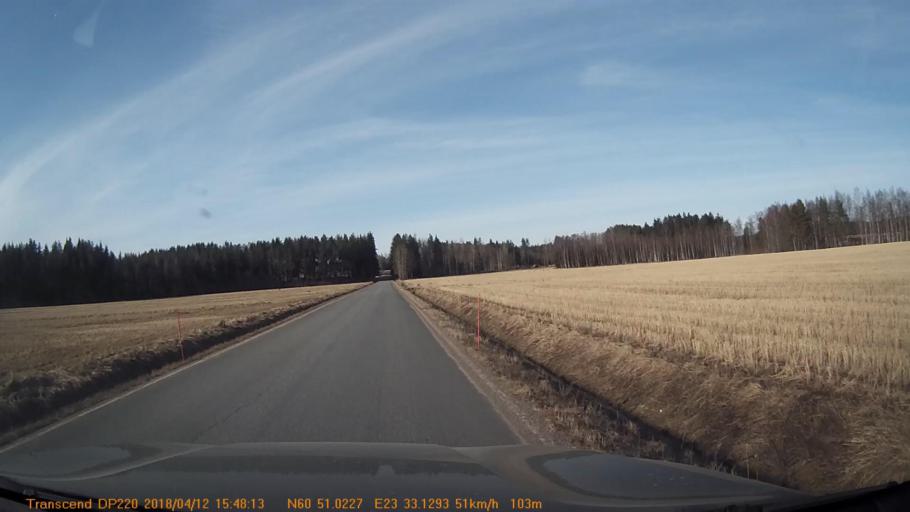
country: FI
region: Haeme
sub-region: Forssa
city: Forssa
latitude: 60.8506
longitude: 23.5520
